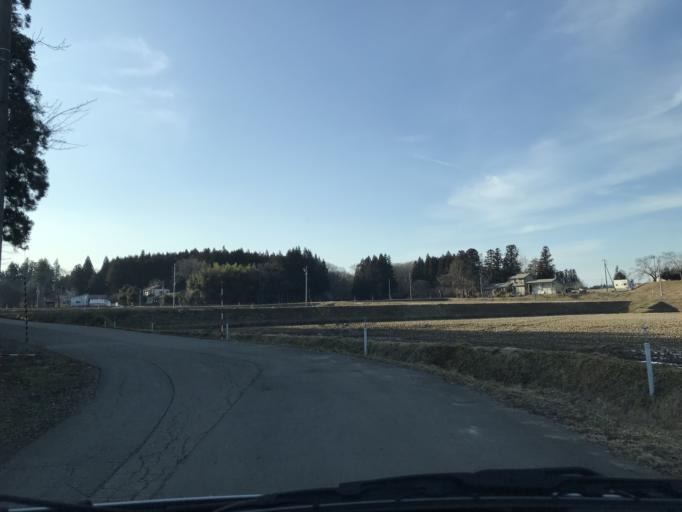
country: JP
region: Iwate
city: Kitakami
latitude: 39.2291
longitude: 141.0641
